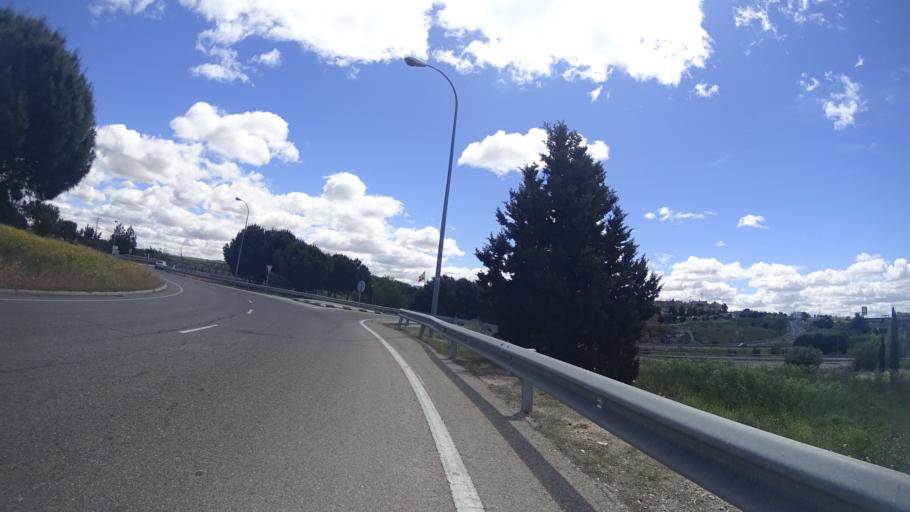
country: ES
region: Madrid
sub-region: Provincia de Madrid
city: Villaviciosa de Odon
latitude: 40.3656
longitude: -3.9211
